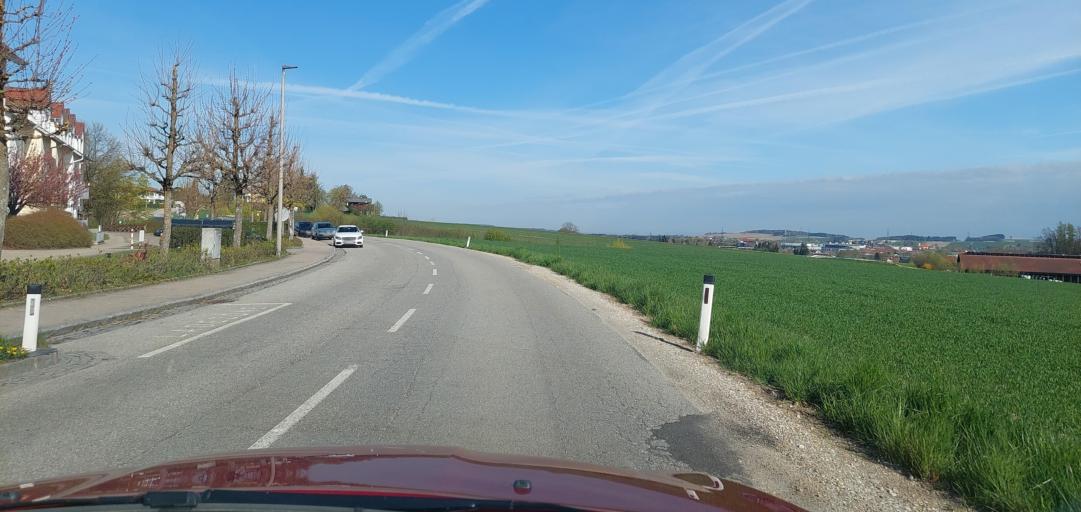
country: AT
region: Upper Austria
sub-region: Politischer Bezirk Ried im Innkreis
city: Ried im Innkreis
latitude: 48.2036
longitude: 13.5036
